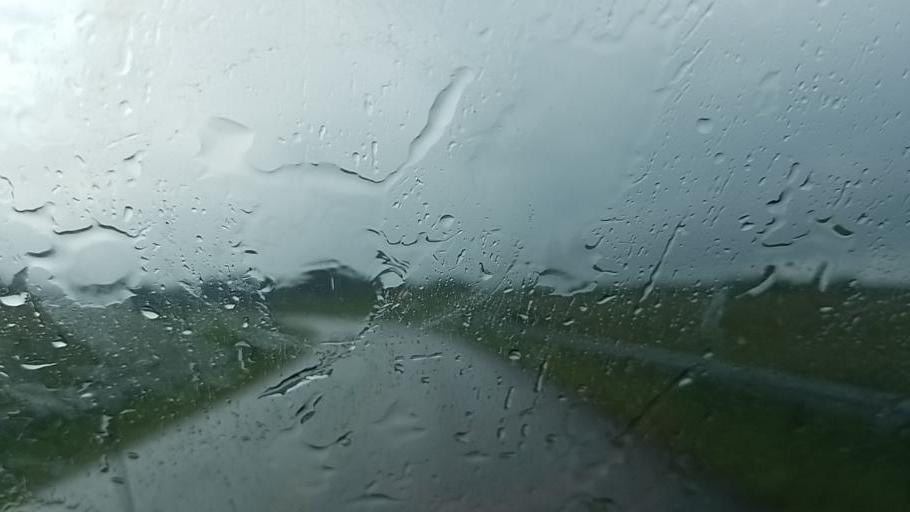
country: US
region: Ohio
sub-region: Champaign County
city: North Lewisburg
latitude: 40.3208
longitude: -83.5957
